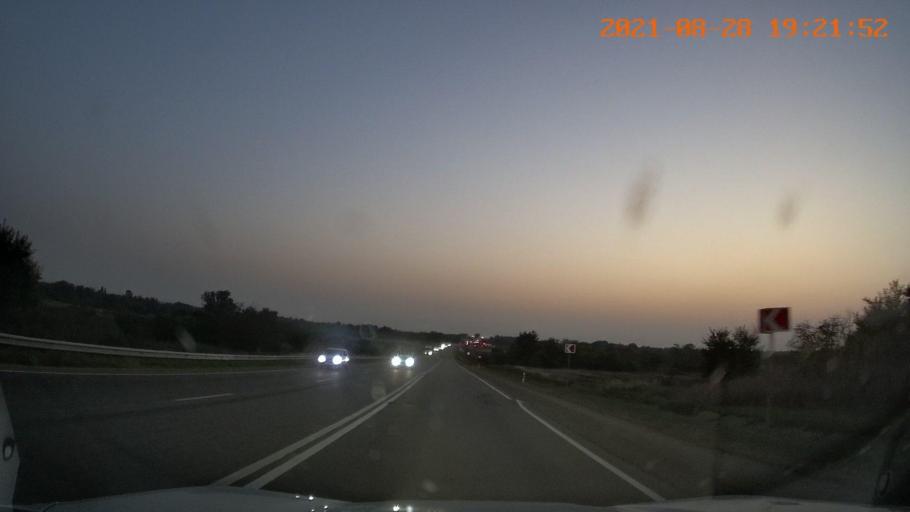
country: RU
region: Adygeya
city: Ponezhukay
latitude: 44.8805
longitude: 39.4725
